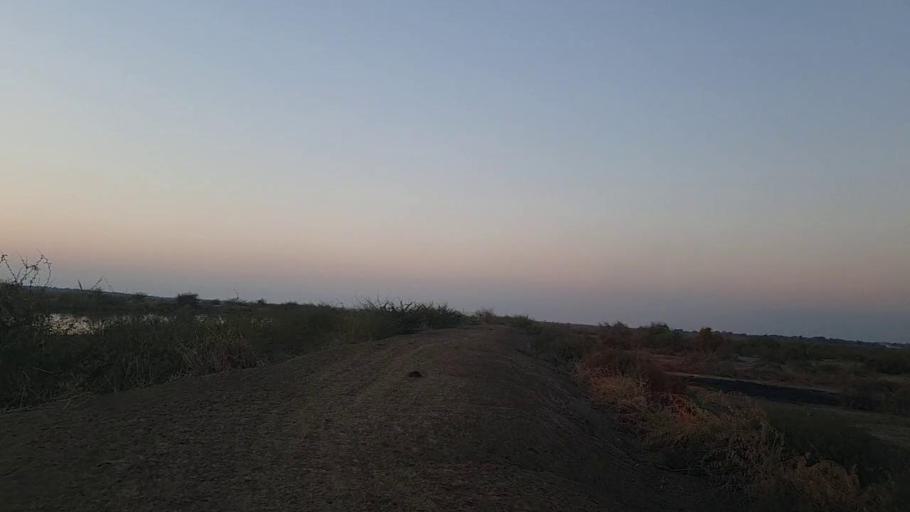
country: PK
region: Sindh
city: Tando Mittha Khan
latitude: 26.0737
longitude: 69.1550
